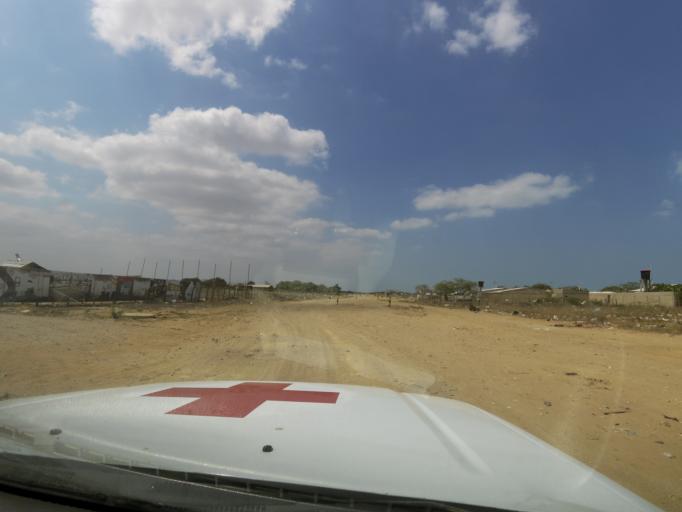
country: CO
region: La Guajira
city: Riohacha
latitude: 11.5223
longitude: -72.9170
